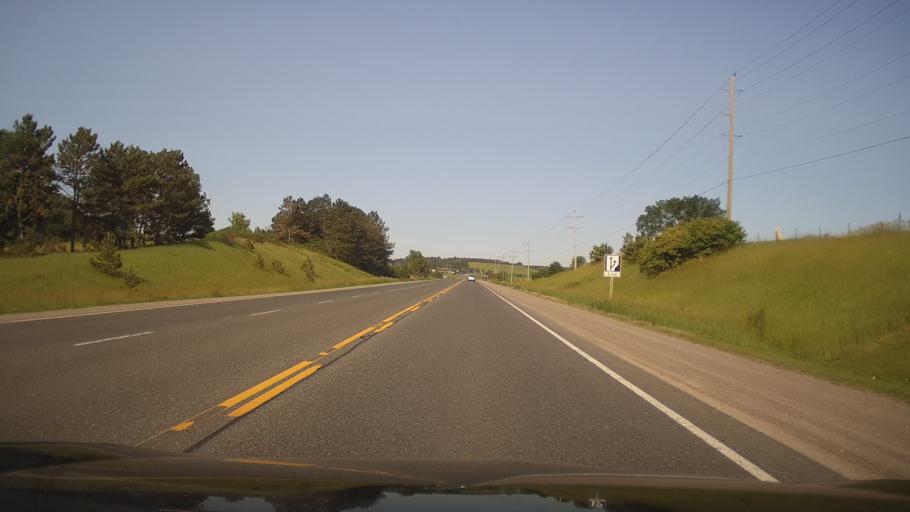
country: CA
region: Ontario
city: Peterborough
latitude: 44.3517
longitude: -78.0607
